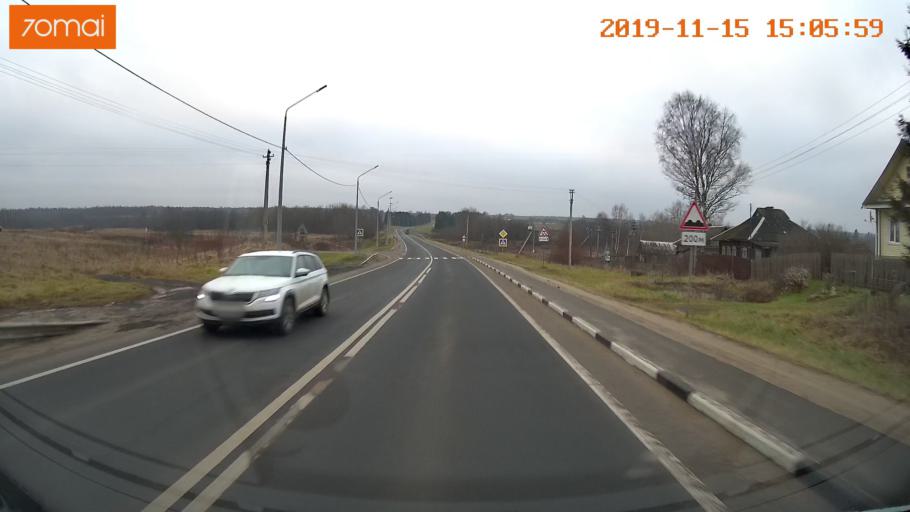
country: RU
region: Jaroslavl
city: Prechistoye
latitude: 58.3978
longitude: 40.3168
